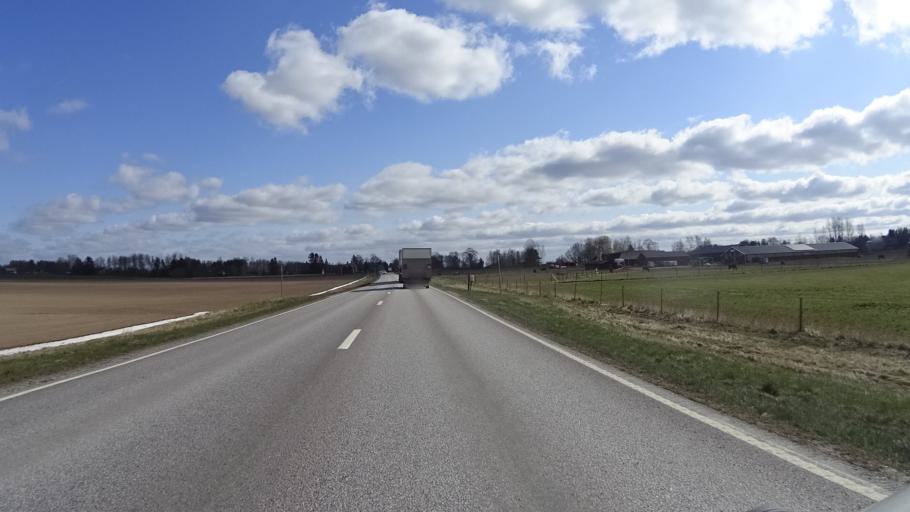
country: SE
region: OEstergoetland
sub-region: Mjolby Kommun
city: Mantorp
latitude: 58.3775
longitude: 15.2412
